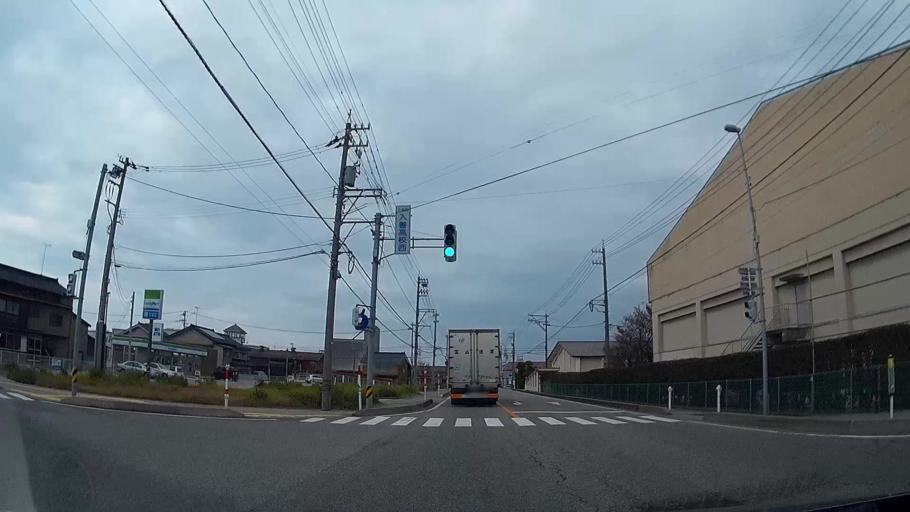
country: JP
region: Toyama
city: Nyuzen
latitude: 36.9343
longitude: 137.5043
